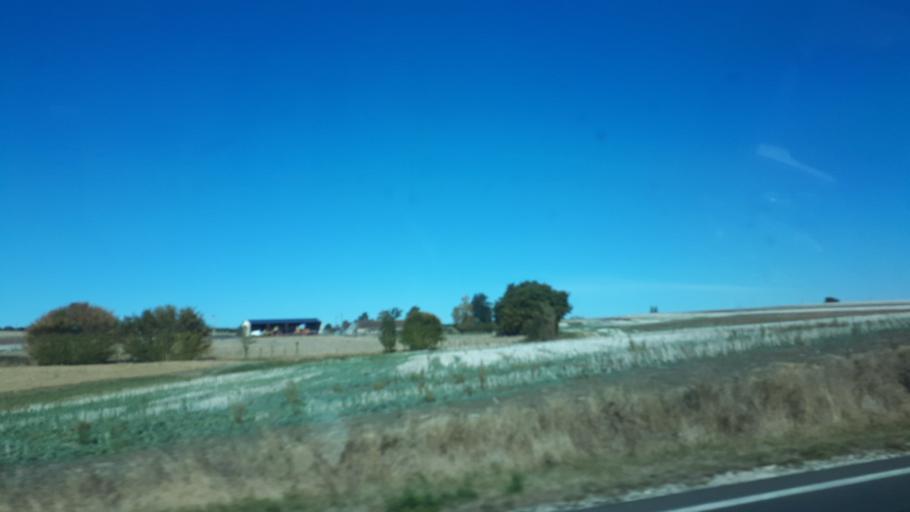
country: FR
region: Centre
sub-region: Departement du Loir-et-Cher
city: Moree
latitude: 47.9407
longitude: 1.2061
